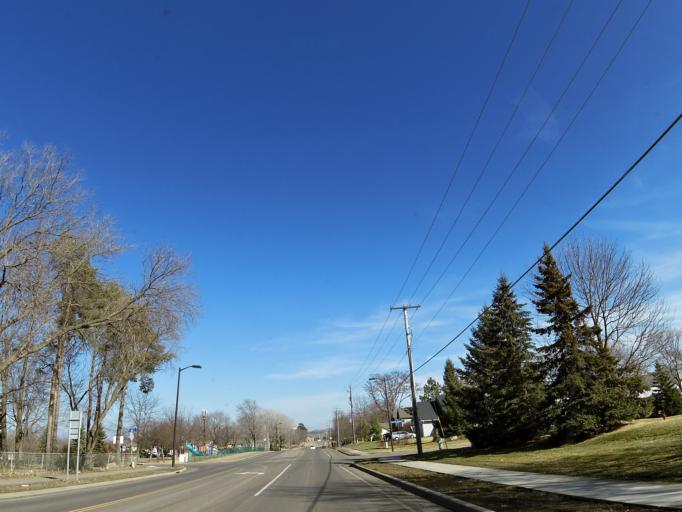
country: US
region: Minnesota
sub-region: Scott County
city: Prior Lake
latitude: 44.7030
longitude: -93.4492
